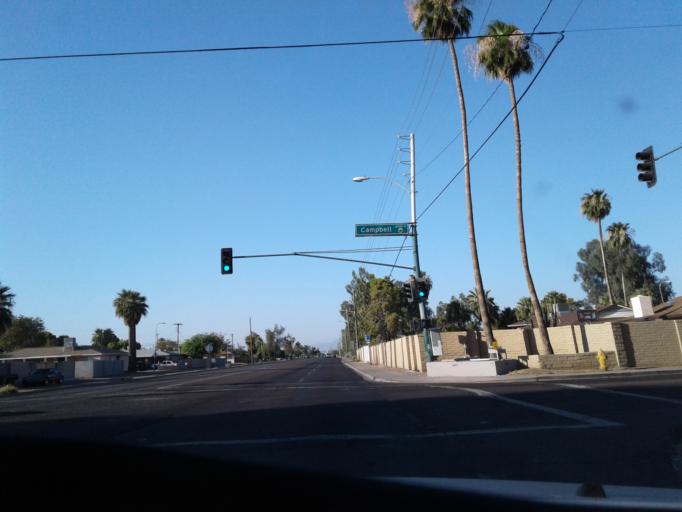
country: US
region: Arizona
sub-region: Maricopa County
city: Glendale
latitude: 33.5023
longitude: -112.1865
